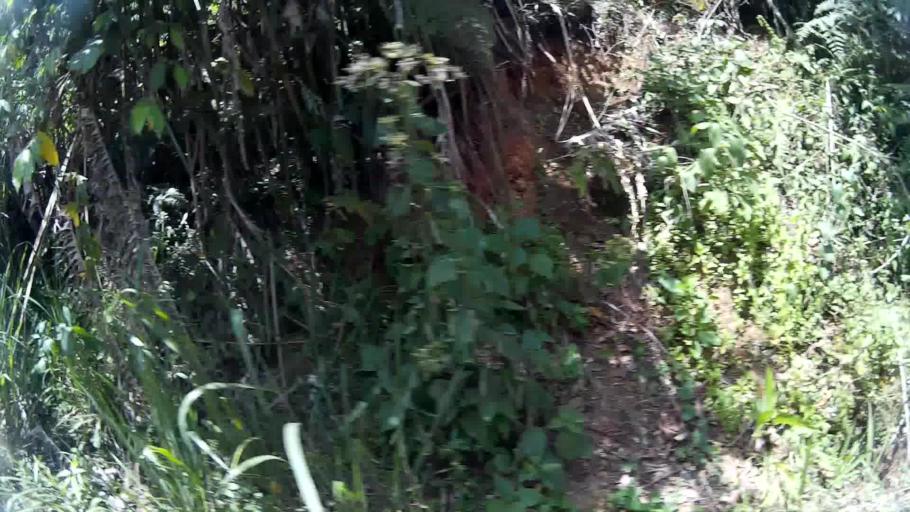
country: CO
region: Risaralda
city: La Virginia
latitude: 4.9409
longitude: -75.8425
